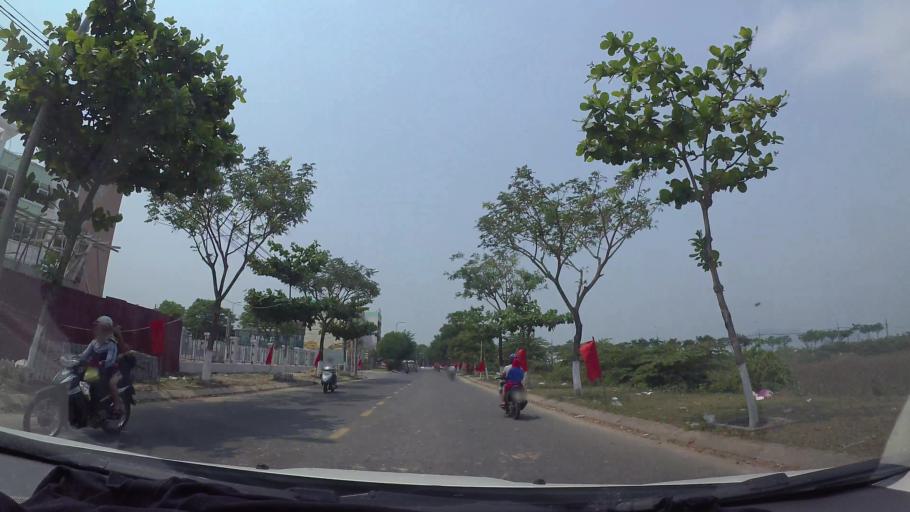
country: VN
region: Da Nang
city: Cam Le
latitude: 16.0060
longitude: 108.2092
